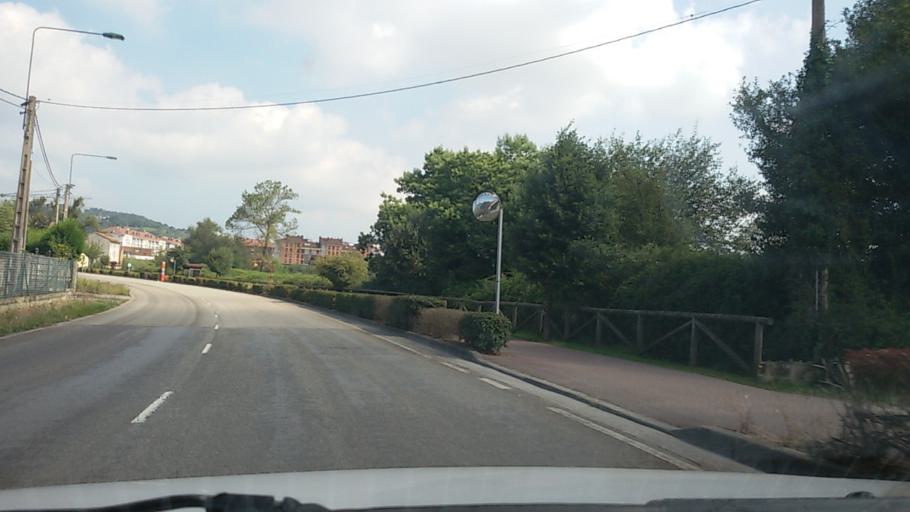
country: ES
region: Asturias
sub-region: Province of Asturias
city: Lugones
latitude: 43.4399
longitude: -5.8249
